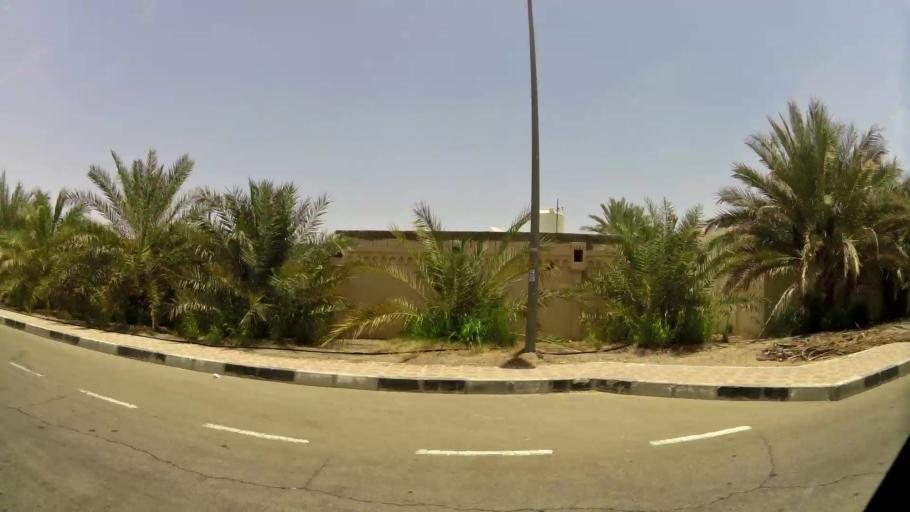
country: OM
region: Al Buraimi
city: Al Buraymi
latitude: 24.2739
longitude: 55.7350
